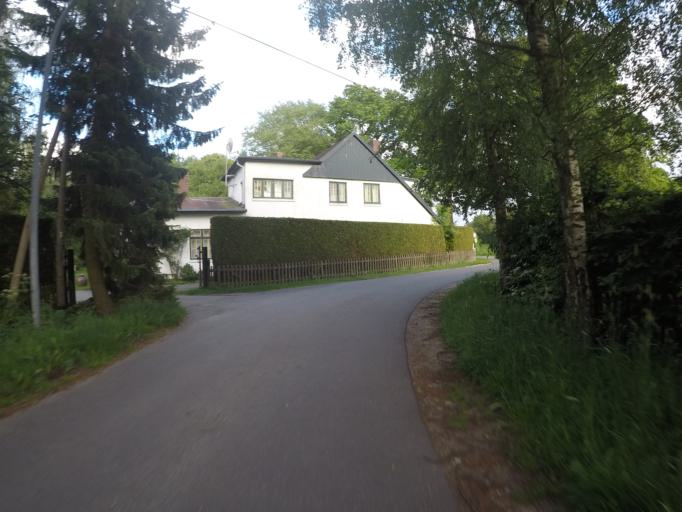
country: DE
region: Schleswig-Holstein
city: Bonningstedt
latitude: 53.6655
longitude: 9.9264
